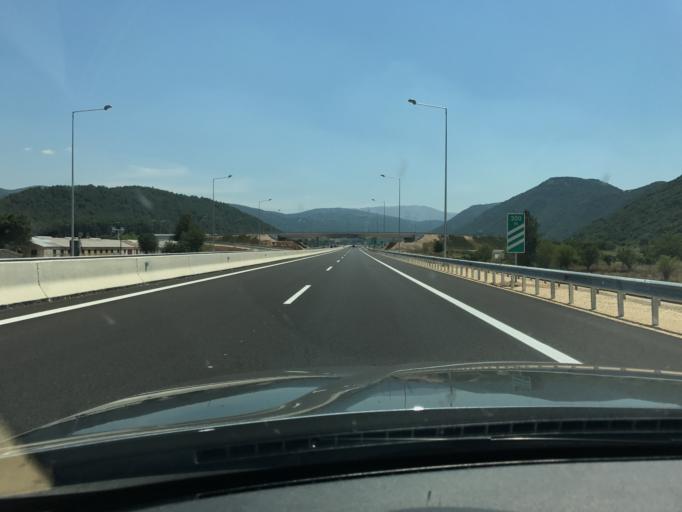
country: GR
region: Epirus
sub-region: Nomos Ioanninon
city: Agia Kyriaki
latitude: 39.5364
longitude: 20.8689
